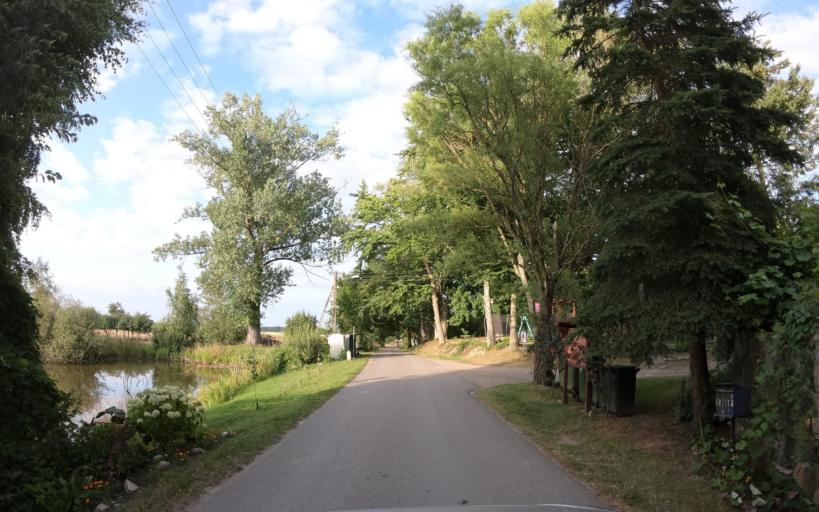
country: PL
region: West Pomeranian Voivodeship
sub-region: Powiat drawski
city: Czaplinek
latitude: 53.5474
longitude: 16.1625
